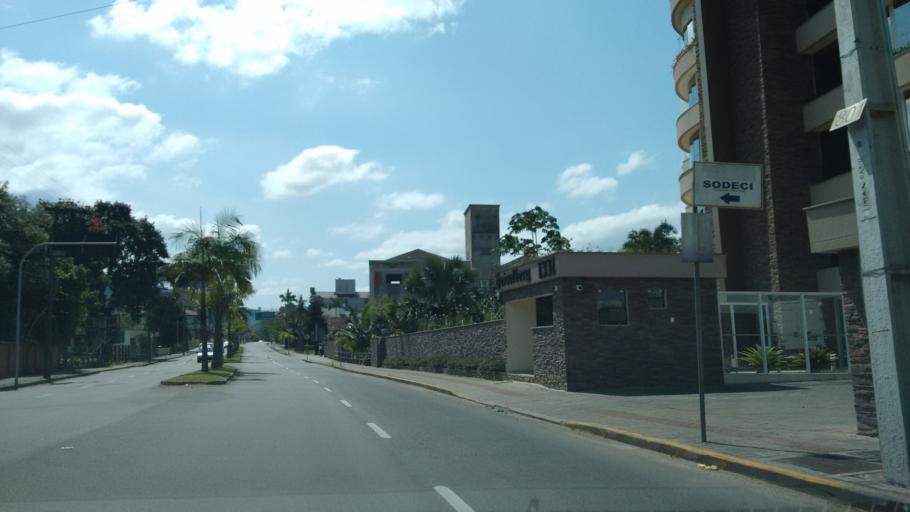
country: BR
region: Santa Catarina
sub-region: Pomerode
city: Pomerode
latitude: -26.7353
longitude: -49.1786
